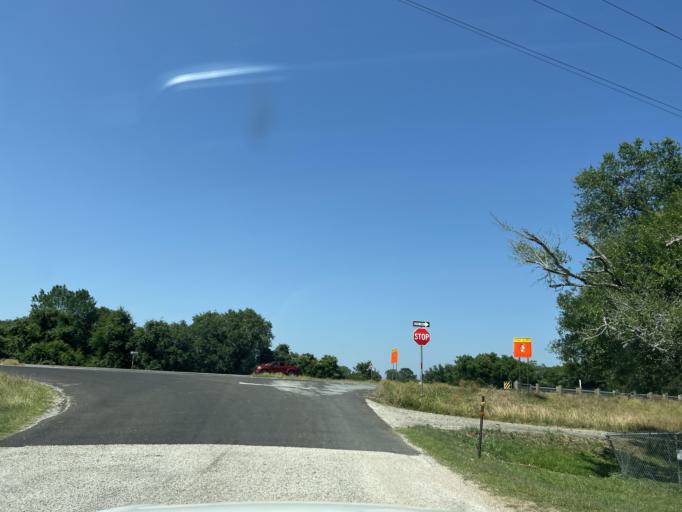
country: US
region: Texas
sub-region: Washington County
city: Brenham
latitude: 30.1828
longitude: -96.4844
